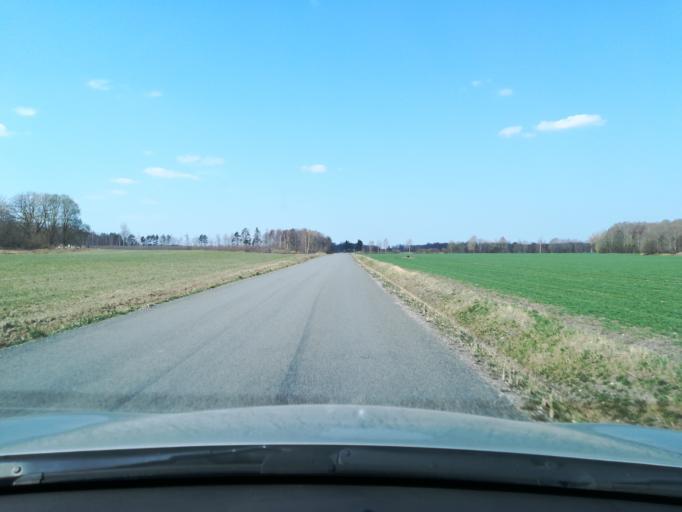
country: EE
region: Harju
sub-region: Saue linn
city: Saue
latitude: 59.3307
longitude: 24.5184
